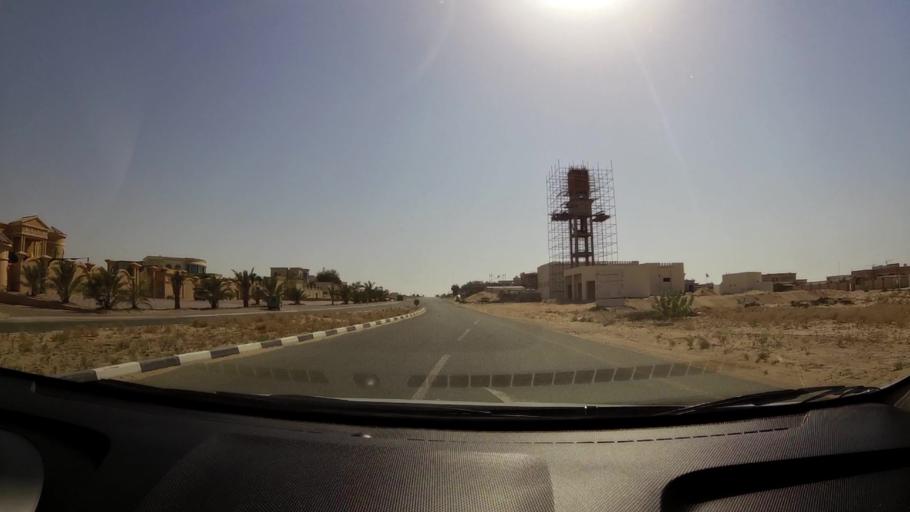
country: AE
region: Umm al Qaywayn
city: Umm al Qaywayn
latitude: 25.4963
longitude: 55.5975
